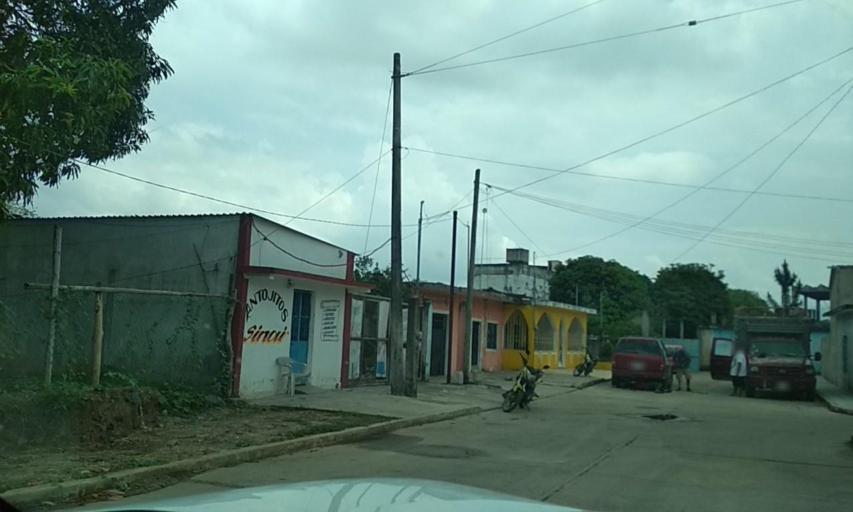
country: MX
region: Veracruz
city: Las Choapas
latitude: 17.8977
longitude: -94.0996
